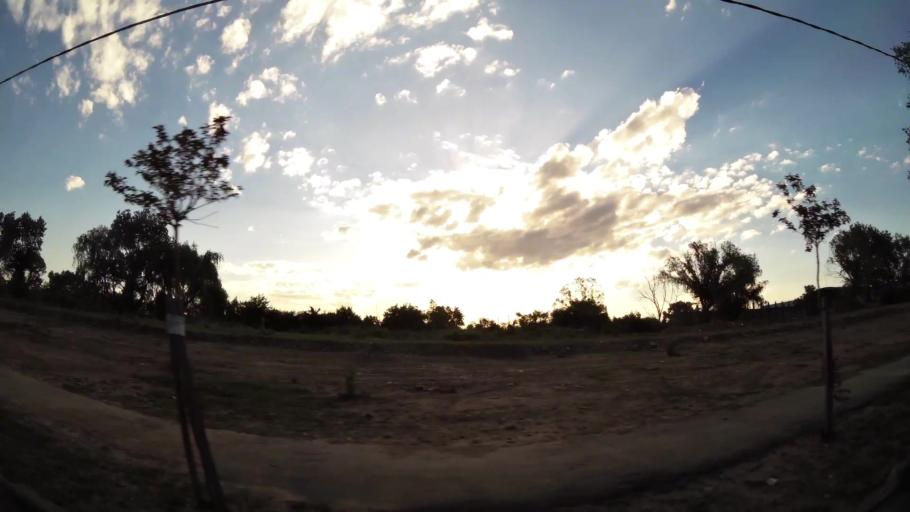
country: AR
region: Buenos Aires
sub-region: Partido de Tigre
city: Tigre
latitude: -34.4566
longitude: -58.5744
